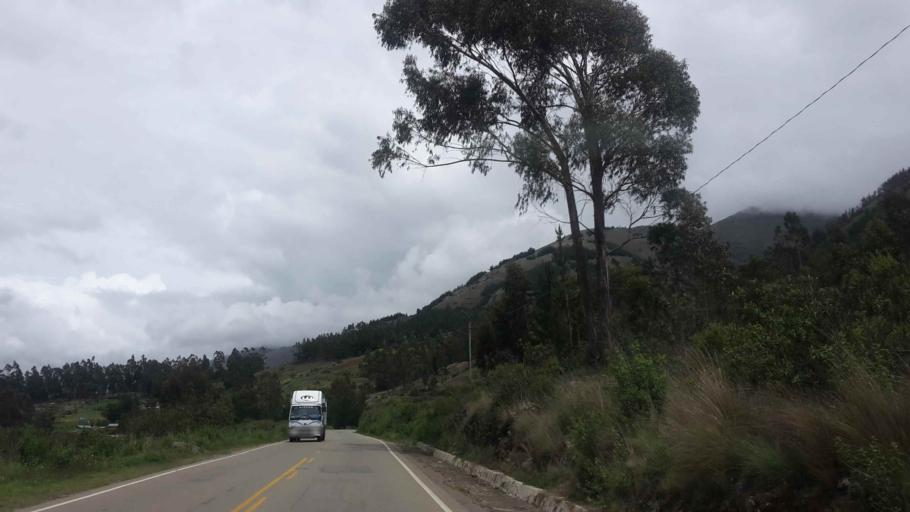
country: BO
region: Cochabamba
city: Arani
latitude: -17.4936
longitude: -65.4491
